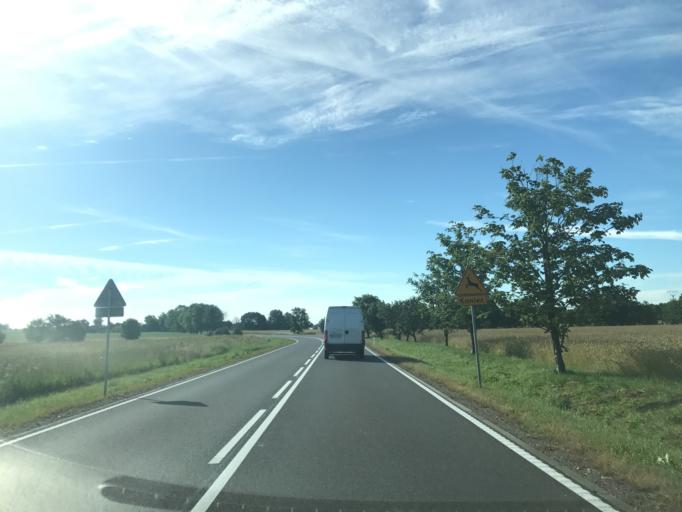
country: PL
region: Pomeranian Voivodeship
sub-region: Powiat czluchowski
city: Rzeczenica
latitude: 53.7435
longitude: 17.1767
